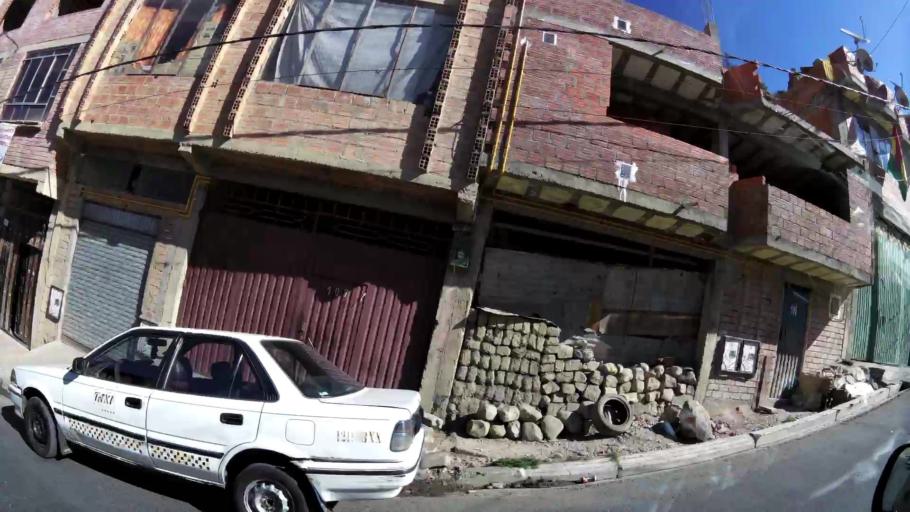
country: BO
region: La Paz
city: La Paz
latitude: -16.5195
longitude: -68.1406
